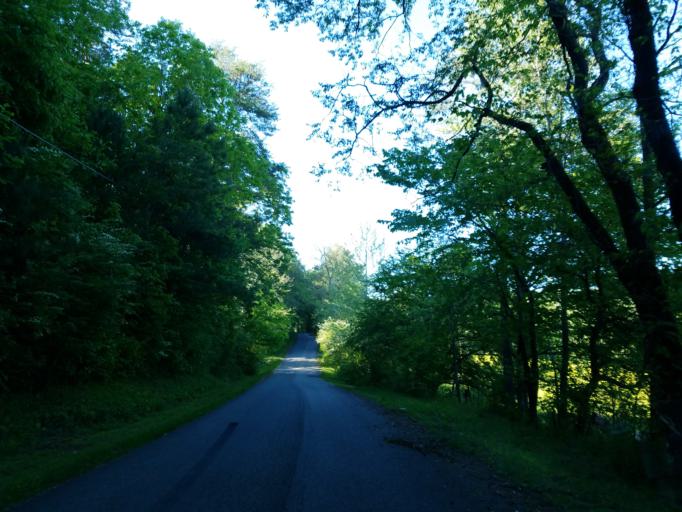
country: US
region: Georgia
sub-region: Gilmer County
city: Ellijay
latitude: 34.5804
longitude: -84.5099
